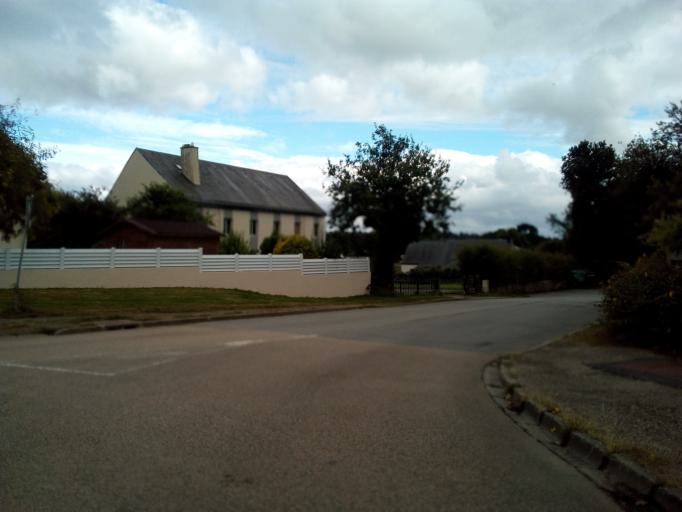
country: FR
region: Brittany
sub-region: Departement du Finistere
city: Landivisiau
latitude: 48.5131
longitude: -4.0577
